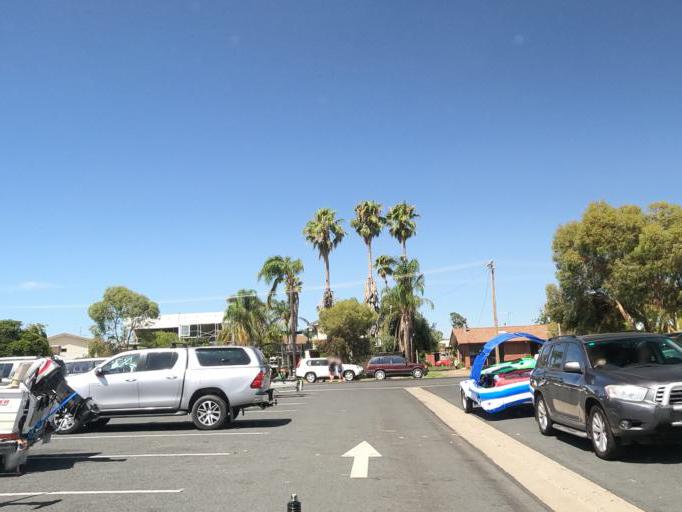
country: AU
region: New South Wales
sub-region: Corowa Shire
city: Mulwala
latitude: -35.9896
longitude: 146.0062
